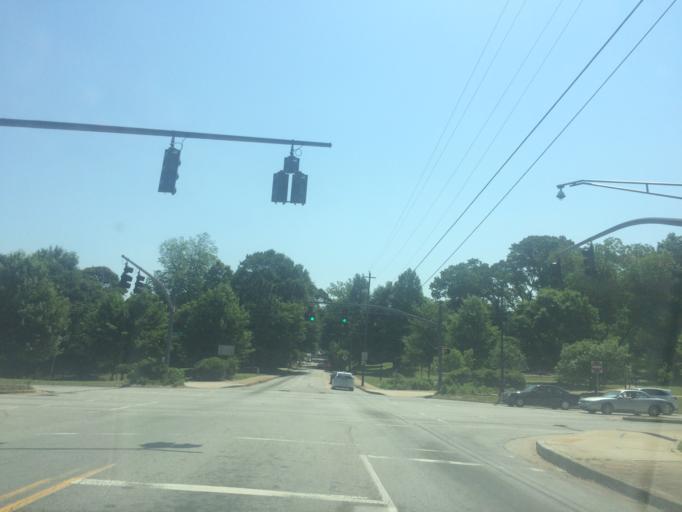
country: US
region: Georgia
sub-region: DeKalb County
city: Druid Hills
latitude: 33.7711
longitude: -84.3598
